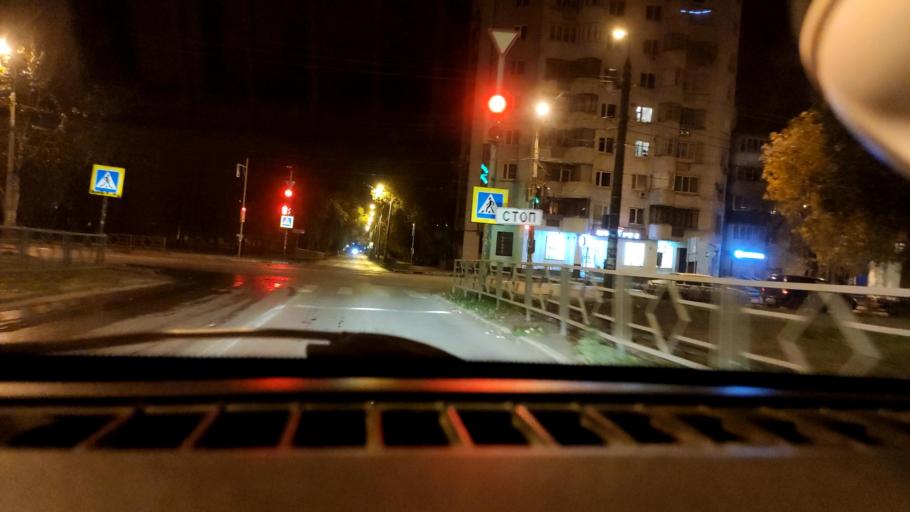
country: RU
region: Samara
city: Samara
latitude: 53.1918
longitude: 50.1840
